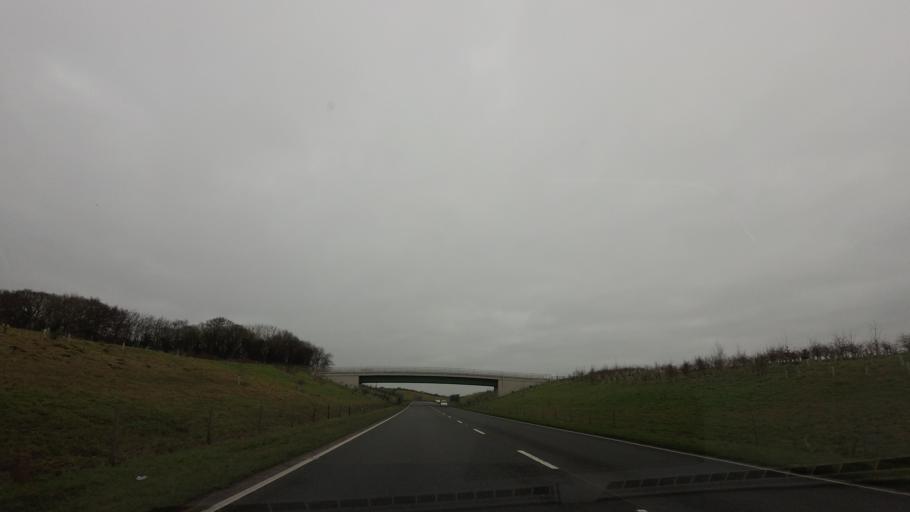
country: GB
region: England
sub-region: East Sussex
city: Bexhill-on-Sea
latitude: 50.8653
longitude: 0.4857
